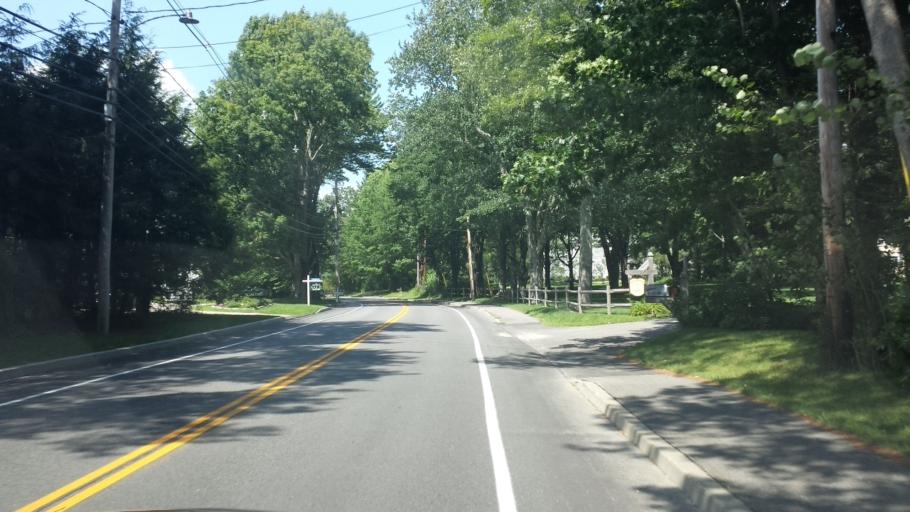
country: US
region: Maine
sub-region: York County
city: Kennebunkport
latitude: 43.3702
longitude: -70.4731
